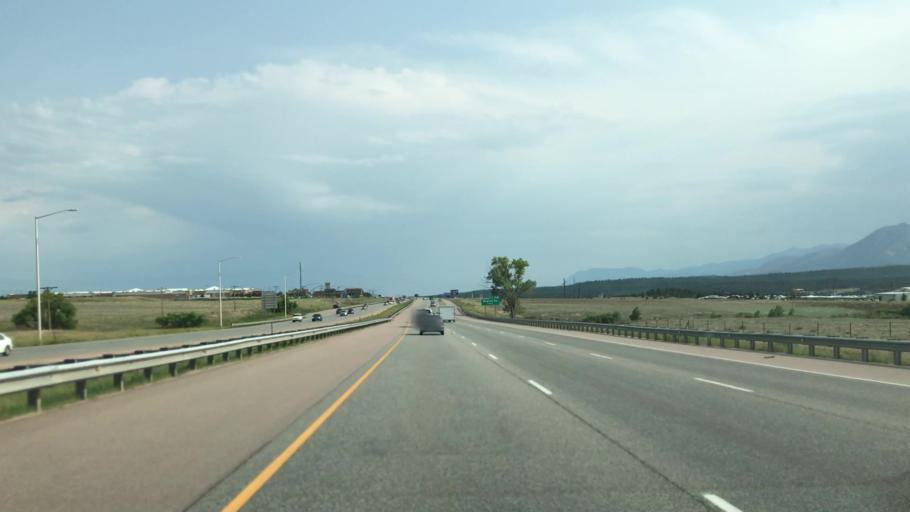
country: US
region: Colorado
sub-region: El Paso County
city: Monument
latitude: 39.0743
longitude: -104.8589
